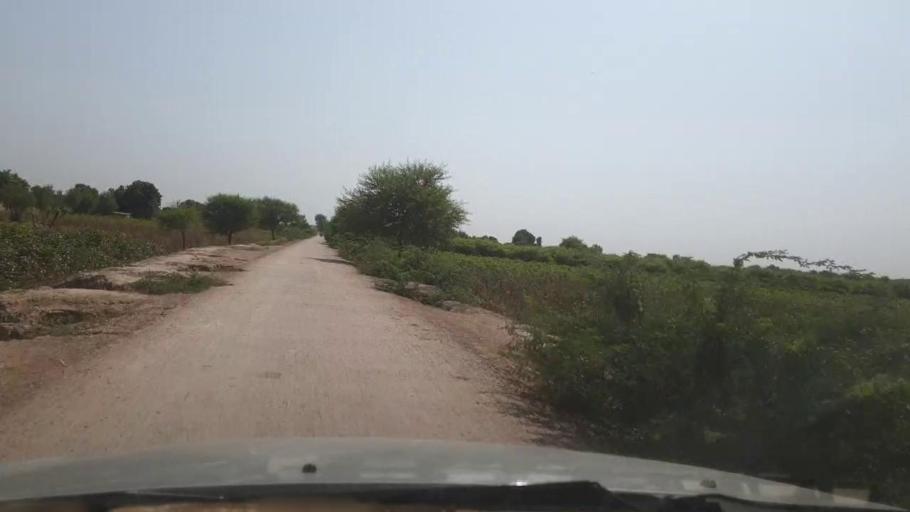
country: PK
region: Sindh
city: Tando Ghulam Ali
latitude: 25.1579
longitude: 68.8950
